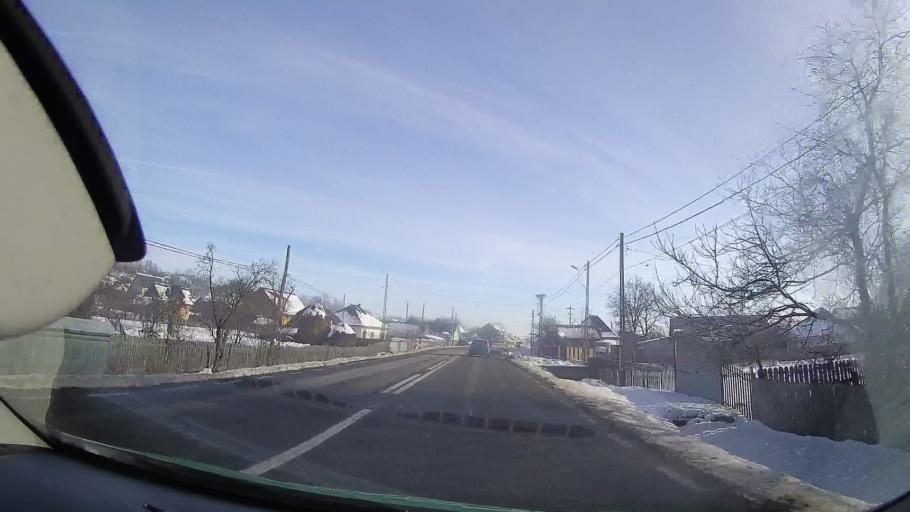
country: RO
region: Neamt
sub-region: Comuna Cracaoani
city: Cracaoani
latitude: 47.0884
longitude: 26.3286
